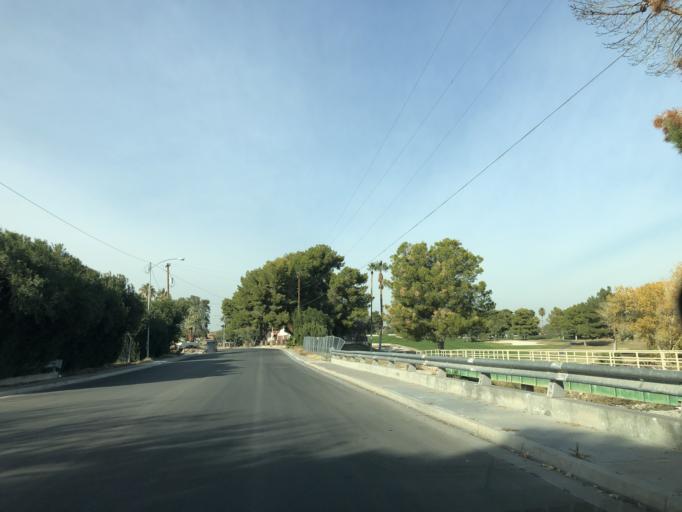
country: US
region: Nevada
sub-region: Clark County
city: Winchester
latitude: 36.1217
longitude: -115.1202
